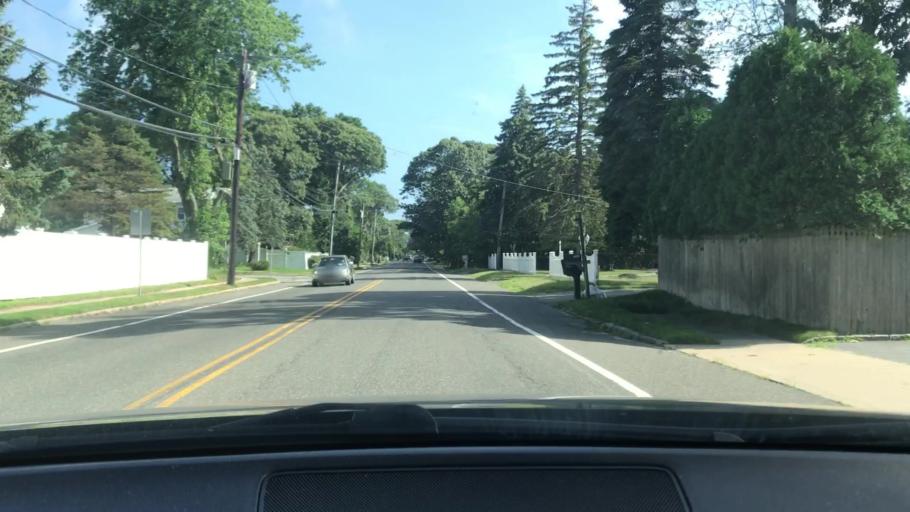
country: US
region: New York
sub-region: Suffolk County
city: Holbrook
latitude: 40.8273
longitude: -73.0810
